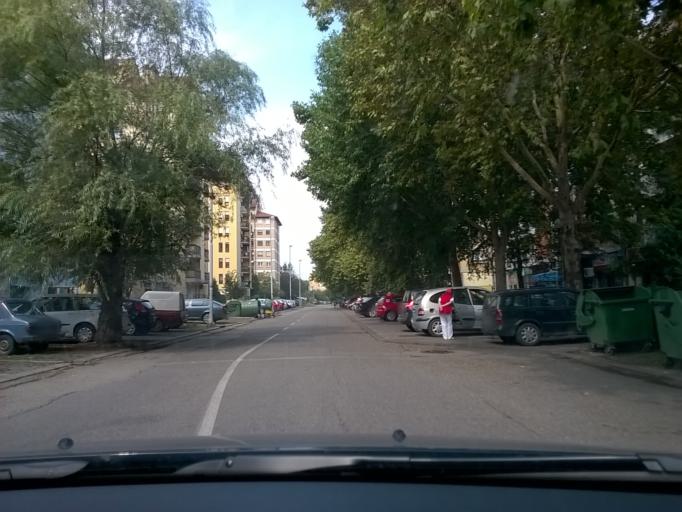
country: RS
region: Autonomna Pokrajina Vojvodina
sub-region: Juznobanatski Okrug
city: Pancevo
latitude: 44.8652
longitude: 20.6666
